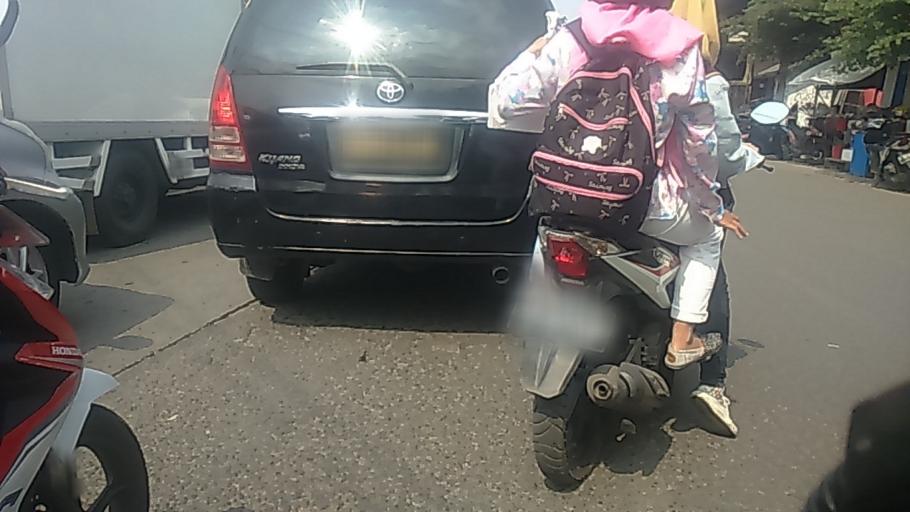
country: ID
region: West Java
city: Depok
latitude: -6.3885
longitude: 106.8195
